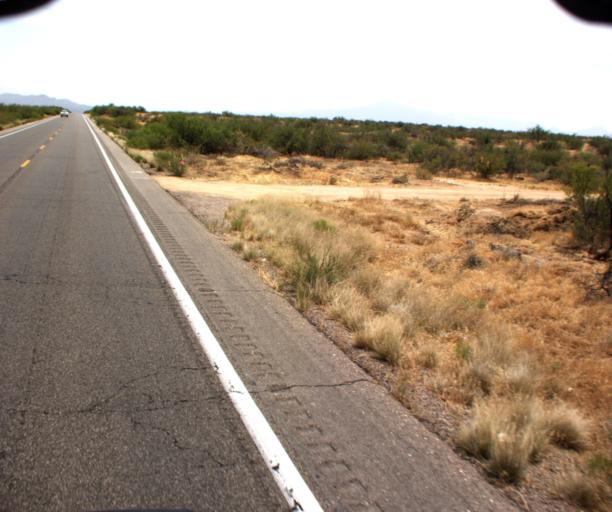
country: US
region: Arizona
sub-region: Gila County
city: Peridot
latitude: 33.3156
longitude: -110.5211
